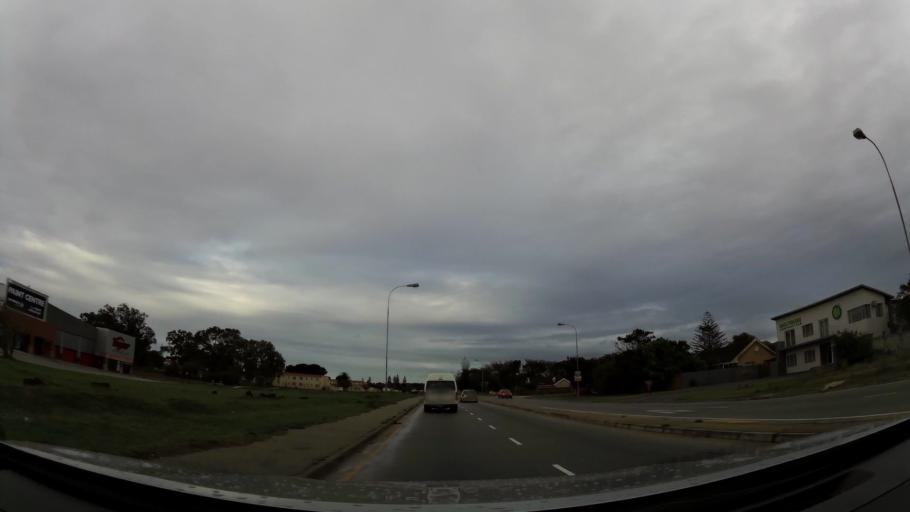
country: ZA
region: Eastern Cape
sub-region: Nelson Mandela Bay Metropolitan Municipality
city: Port Elizabeth
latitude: -33.9849
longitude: 25.5529
